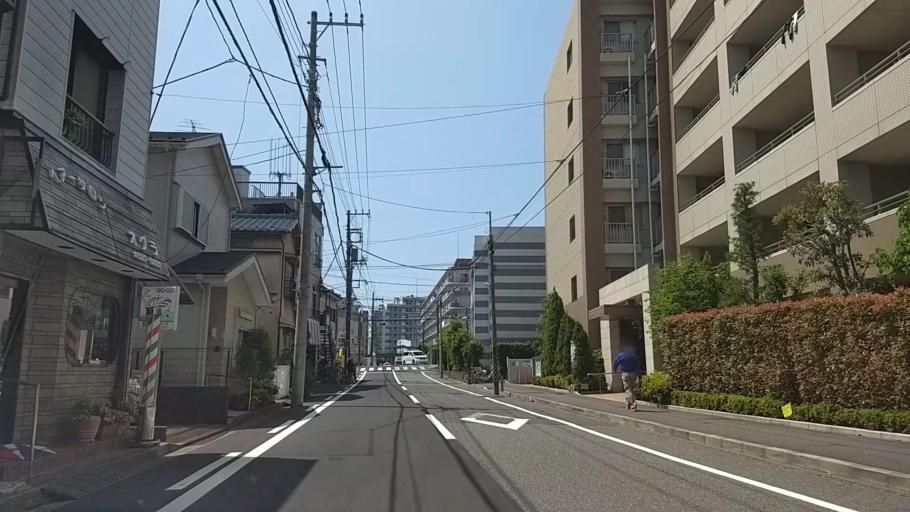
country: JP
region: Kanagawa
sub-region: Kawasaki-shi
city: Kawasaki
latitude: 35.5017
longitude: 139.6797
